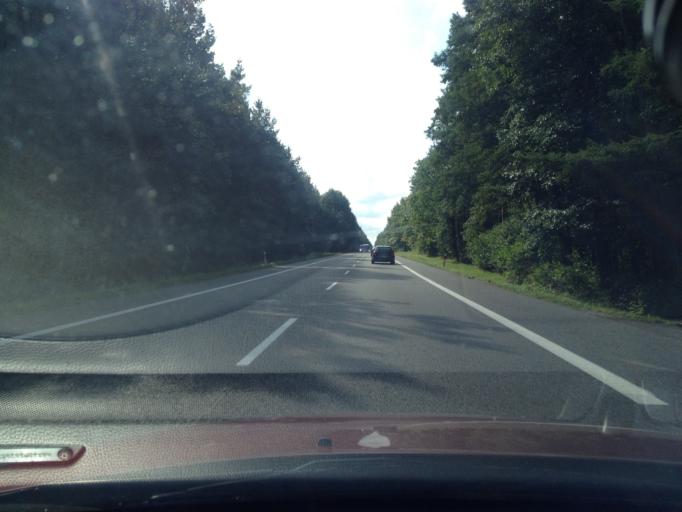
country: PL
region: West Pomeranian Voivodeship
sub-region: Powiat goleniowski
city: Przybiernow
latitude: 53.7846
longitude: 14.7751
